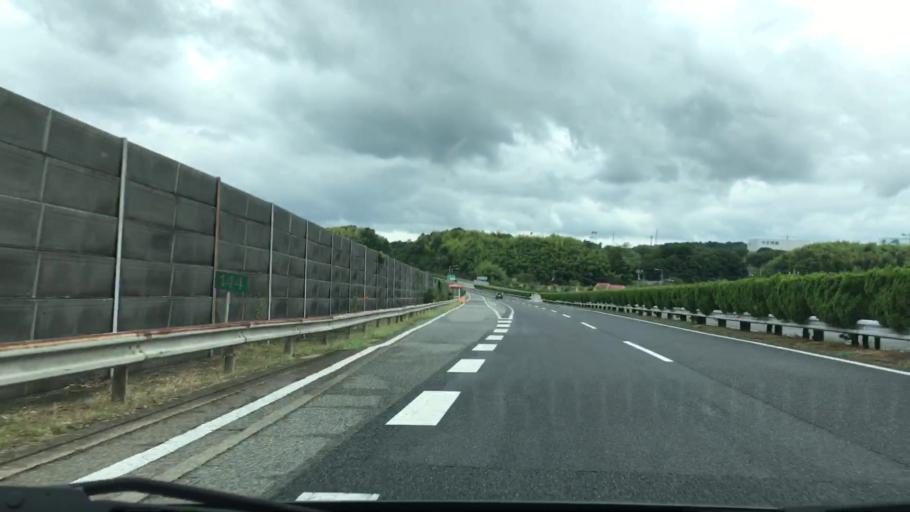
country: JP
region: Okayama
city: Tsuyama
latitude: 35.0433
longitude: 134.1189
